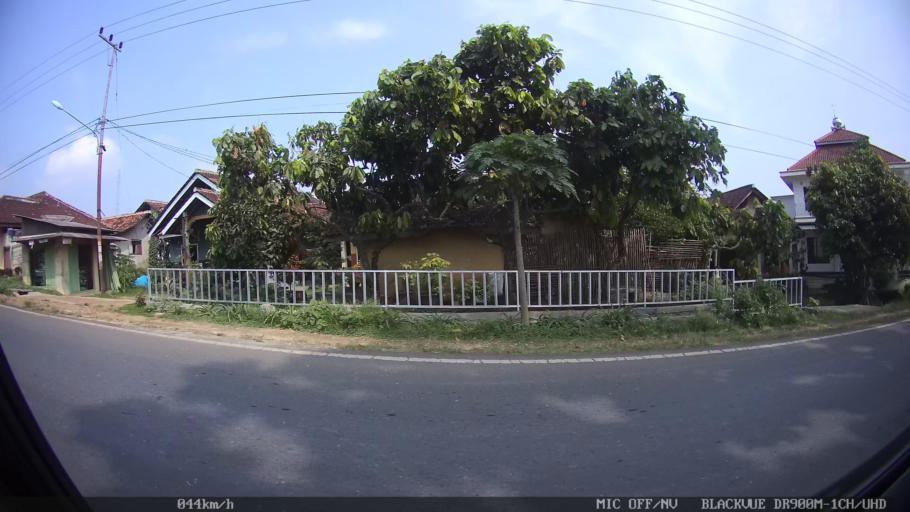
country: ID
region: Lampung
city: Gadingrejo
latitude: -5.3723
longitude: 105.0719
